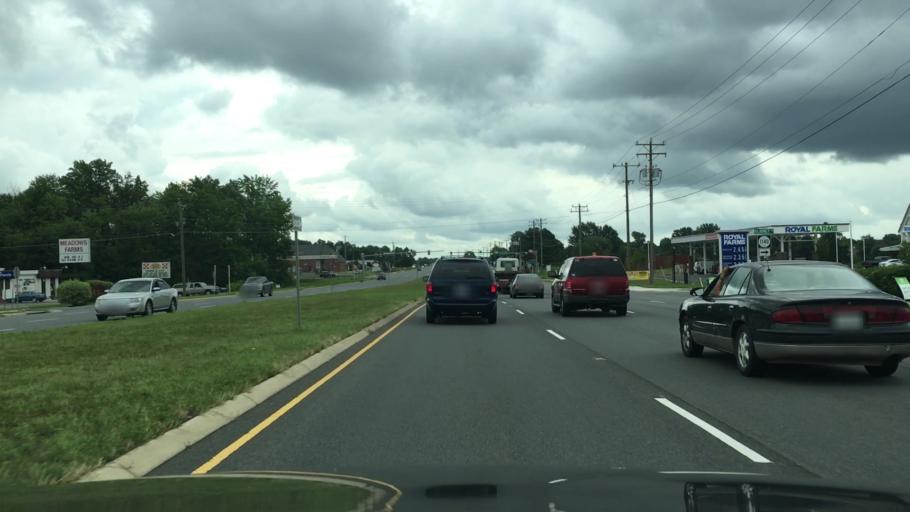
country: US
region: Virginia
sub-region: Stafford County
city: Falmouth
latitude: 38.2898
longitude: -77.5497
